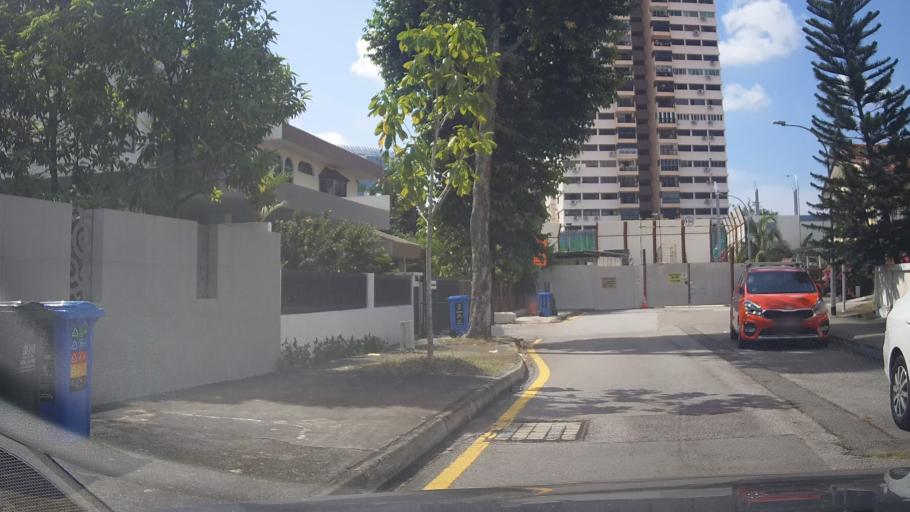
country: SG
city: Singapore
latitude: 1.3106
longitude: 103.9292
